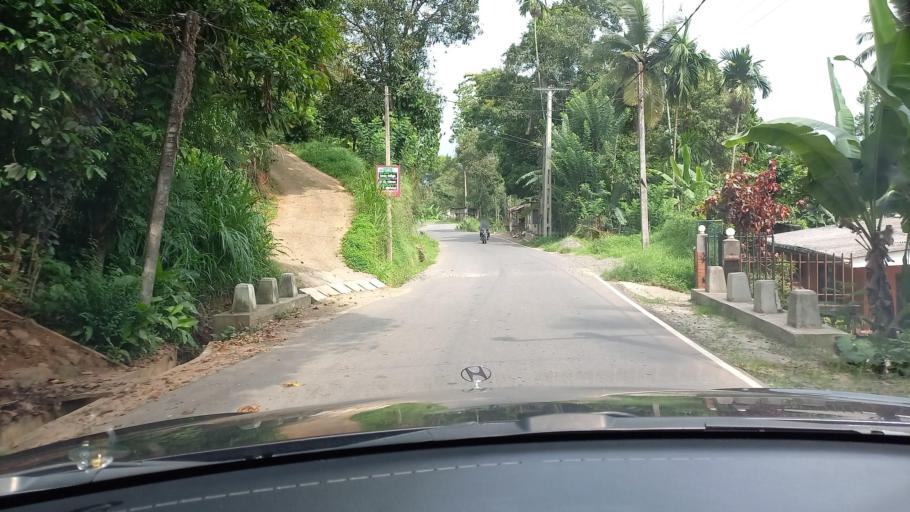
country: LK
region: Central
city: Gampola
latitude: 7.2135
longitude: 80.6146
